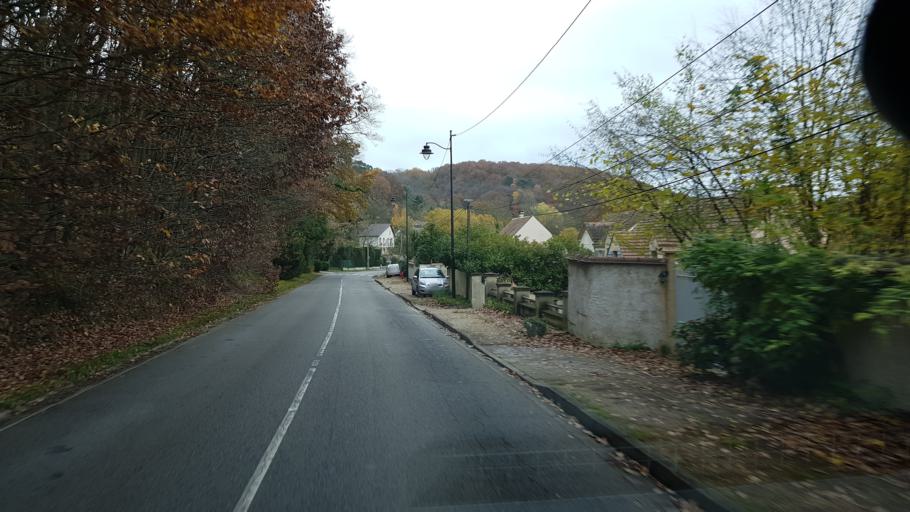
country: FR
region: Ile-de-France
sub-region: Departement des Yvelines
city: Chevreuse
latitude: 48.7130
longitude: 2.0274
